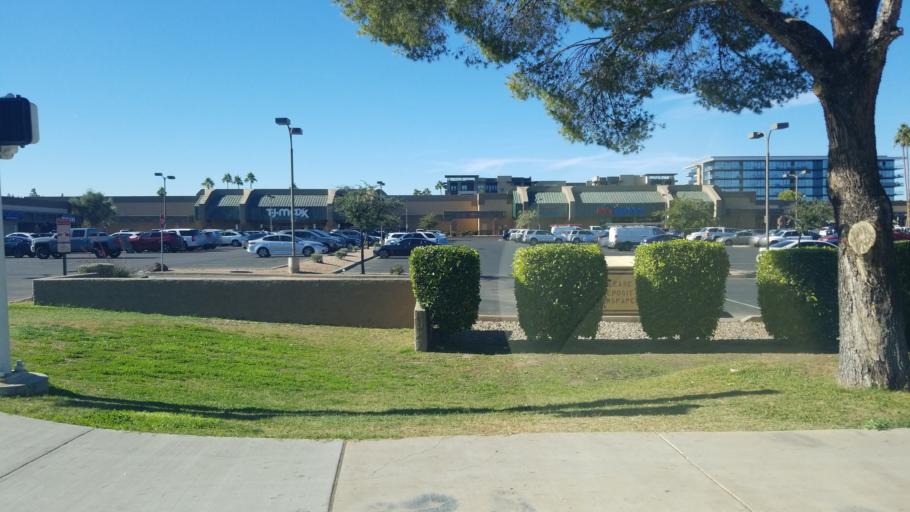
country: US
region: Arizona
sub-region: Maricopa County
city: Scottsdale
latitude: 33.4998
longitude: -111.9176
